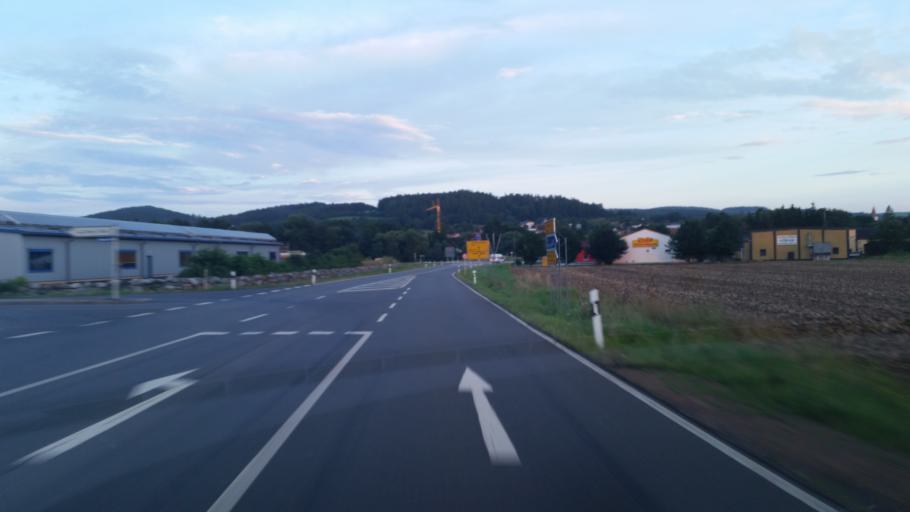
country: DE
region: Bavaria
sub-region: Upper Palatinate
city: Luhe-Wildenau
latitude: 49.5905
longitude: 12.1455
